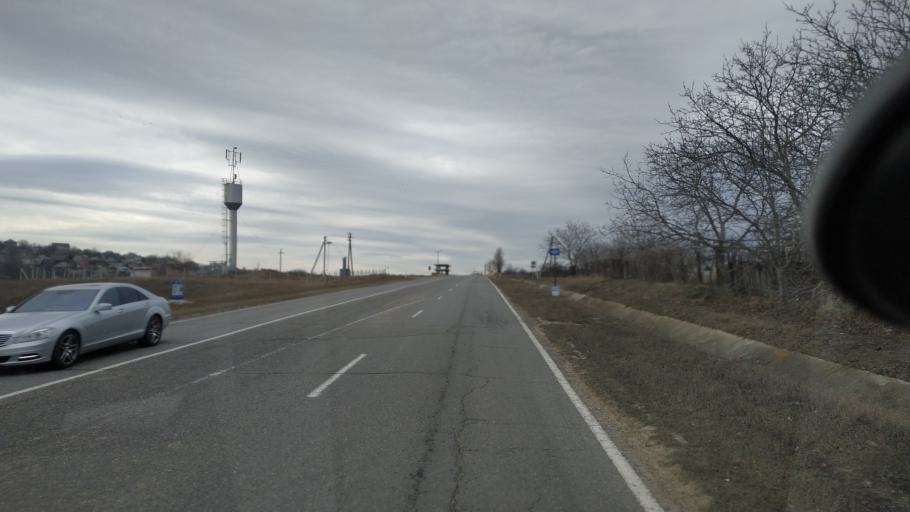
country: MD
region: Chisinau
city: Vadul lui Voda
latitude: 47.0841
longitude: 29.0791
